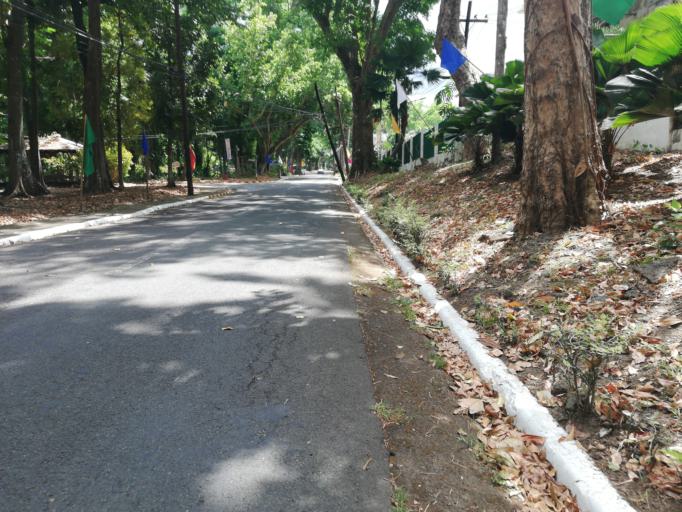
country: PH
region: Calabarzon
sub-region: Province of Laguna
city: Los Banos
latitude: 14.1574
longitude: 121.2363
